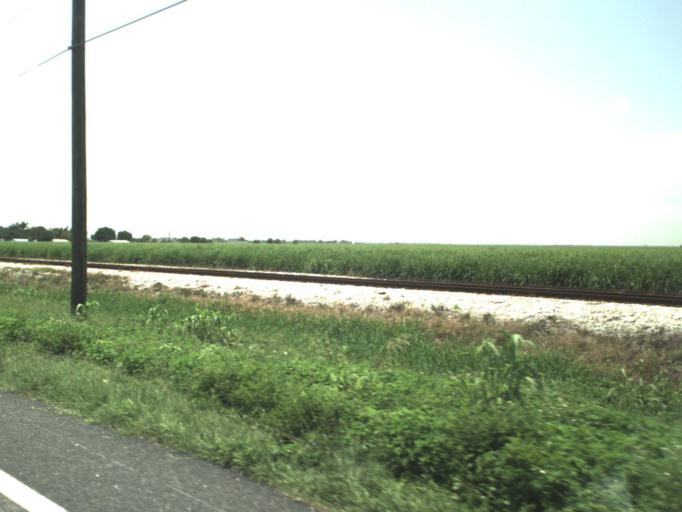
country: US
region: Florida
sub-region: Palm Beach County
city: Belle Glade
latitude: 26.7385
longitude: -80.6628
